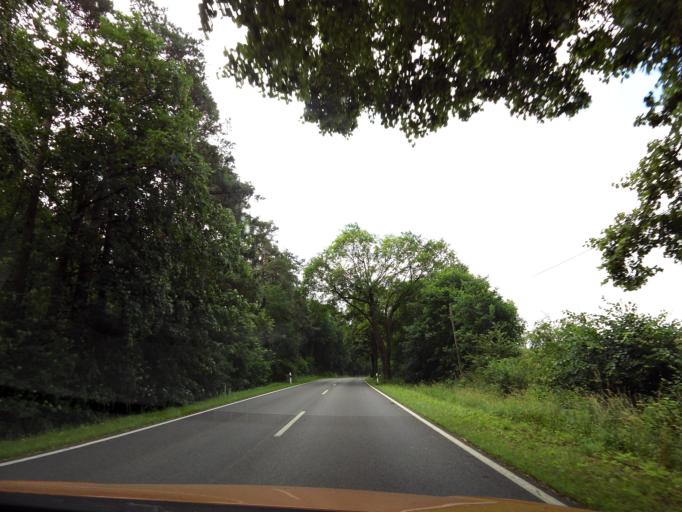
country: DE
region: Mecklenburg-Vorpommern
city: Muhl Rosin
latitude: 53.7692
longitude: 12.2451
